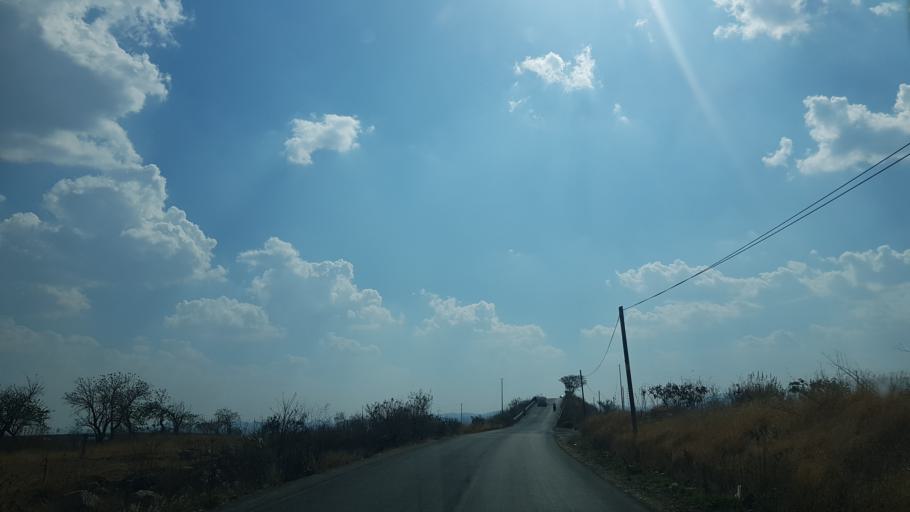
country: MX
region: Puebla
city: Atlixco
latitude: 18.9019
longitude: -98.4884
